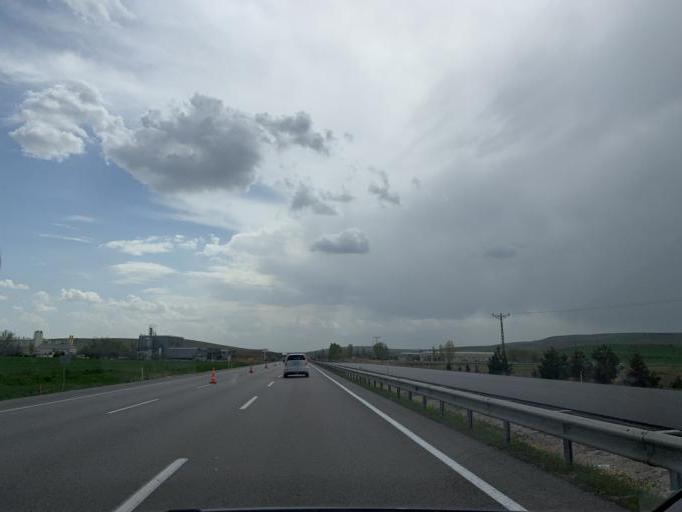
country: TR
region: Ankara
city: Polatli
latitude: 39.6443
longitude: 32.2083
